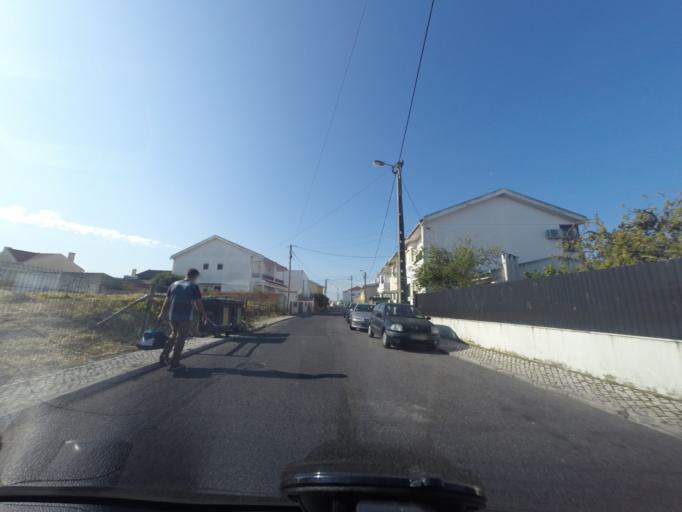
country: PT
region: Lisbon
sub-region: Cascais
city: Sao Domingos de Rana
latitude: 38.7059
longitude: -9.3428
